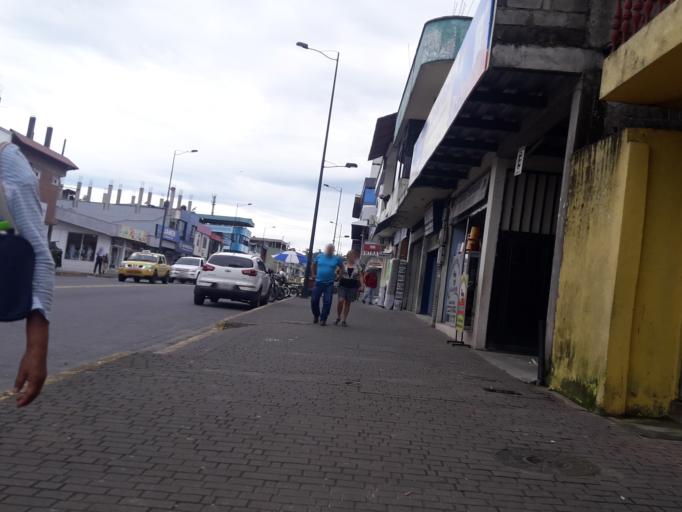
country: EC
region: Napo
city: Tena
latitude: -0.9997
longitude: -77.8120
